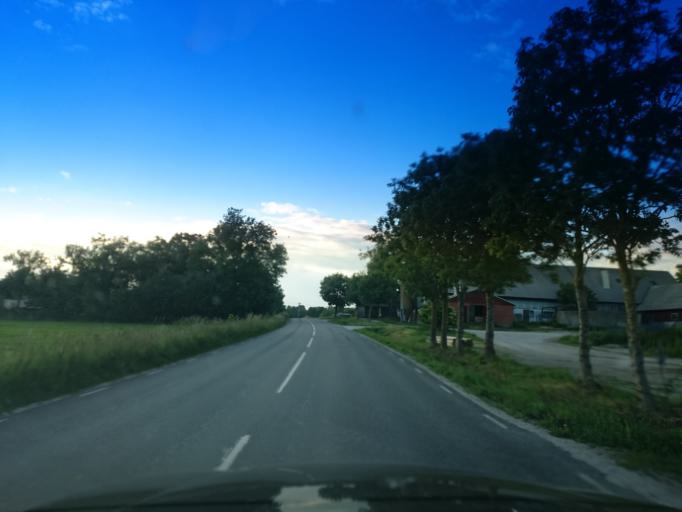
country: SE
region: Gotland
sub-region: Gotland
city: Hemse
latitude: 57.3202
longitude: 18.3853
